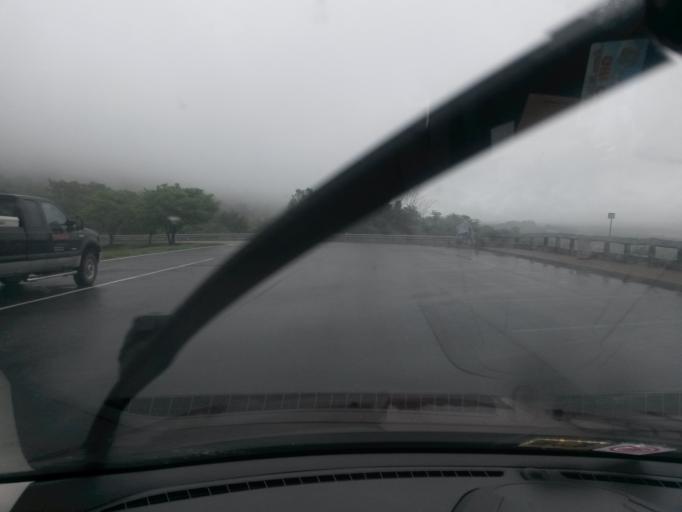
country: US
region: Virginia
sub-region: Augusta County
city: Dooms
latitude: 38.0447
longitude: -78.7921
